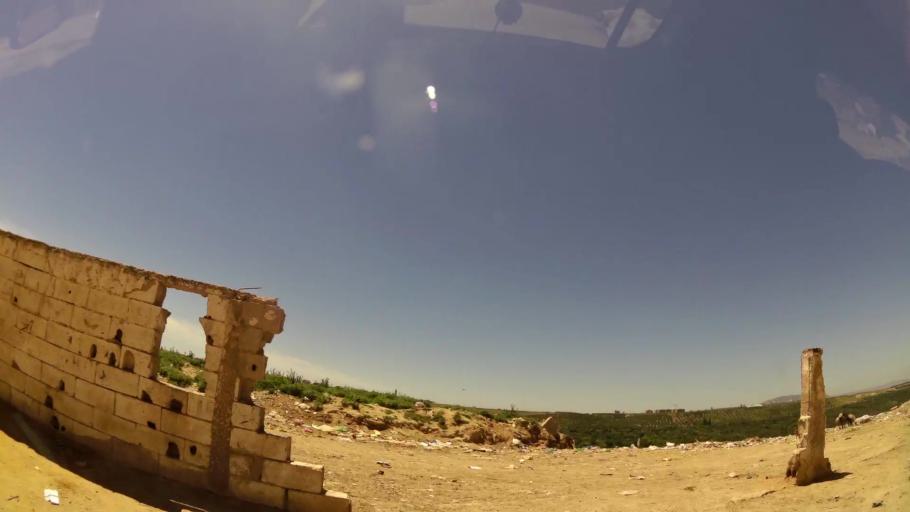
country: MA
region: Meknes-Tafilalet
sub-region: Meknes
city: Meknes
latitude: 33.9101
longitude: -5.5816
